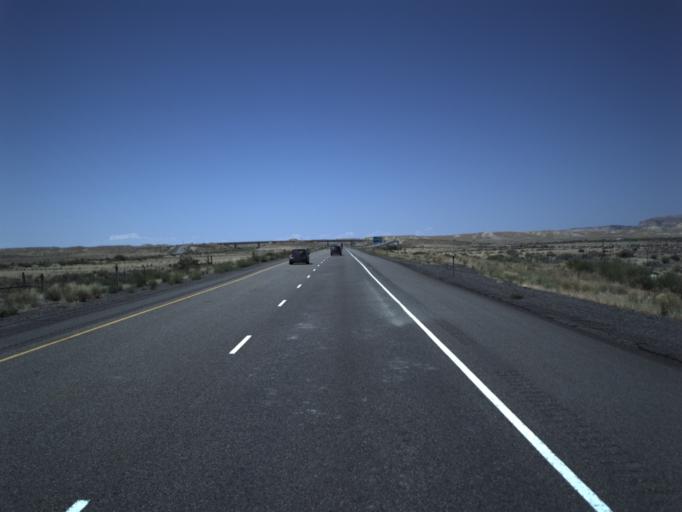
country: US
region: Utah
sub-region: Grand County
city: Moab
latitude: 38.9428
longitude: -109.6029
